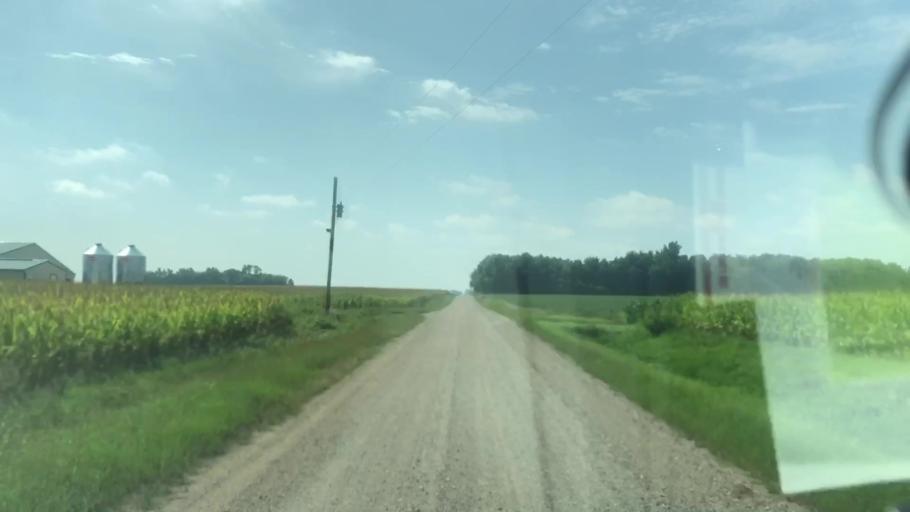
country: US
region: Iowa
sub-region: O'Brien County
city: Sheldon
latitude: 43.1952
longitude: -95.9416
